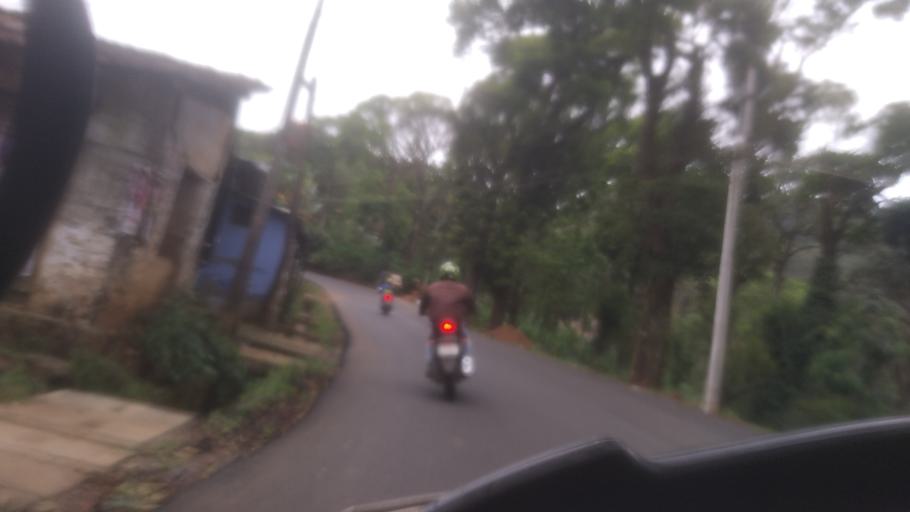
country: IN
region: Tamil Nadu
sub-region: Theni
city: Kombai
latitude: 9.8931
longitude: 77.1432
